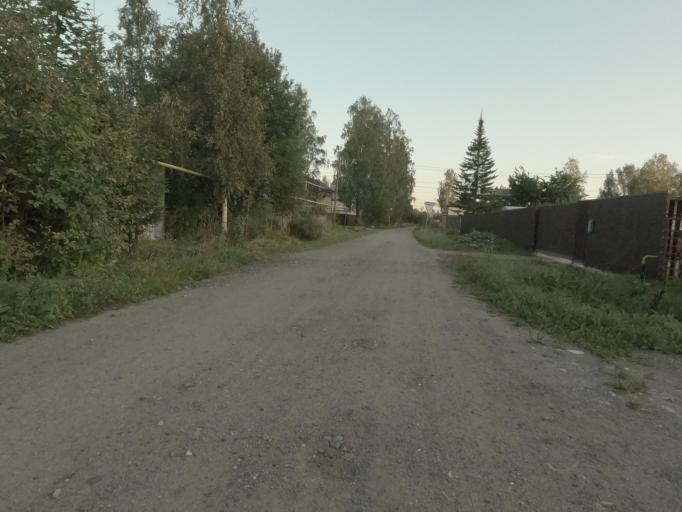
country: RU
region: Leningrad
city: Mga
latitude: 59.7600
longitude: 31.0495
